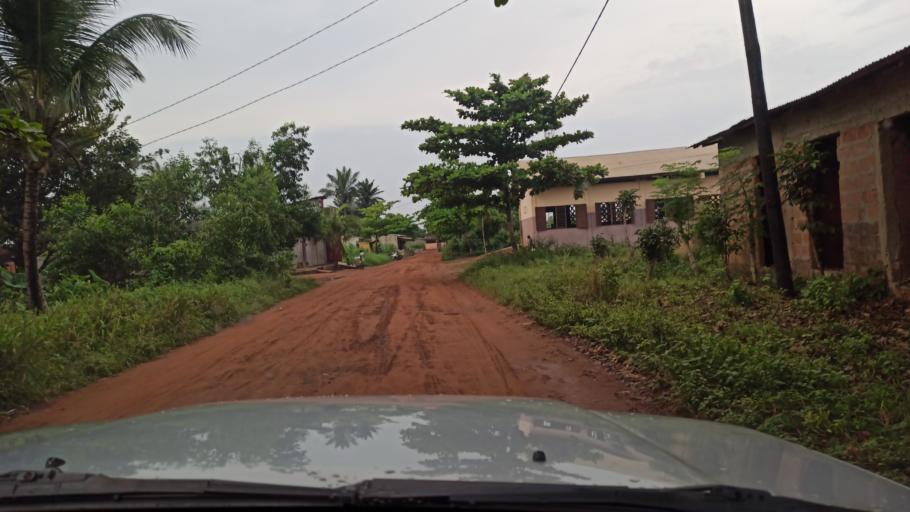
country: BJ
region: Queme
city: Porto-Novo
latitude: 6.4770
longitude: 2.6746
